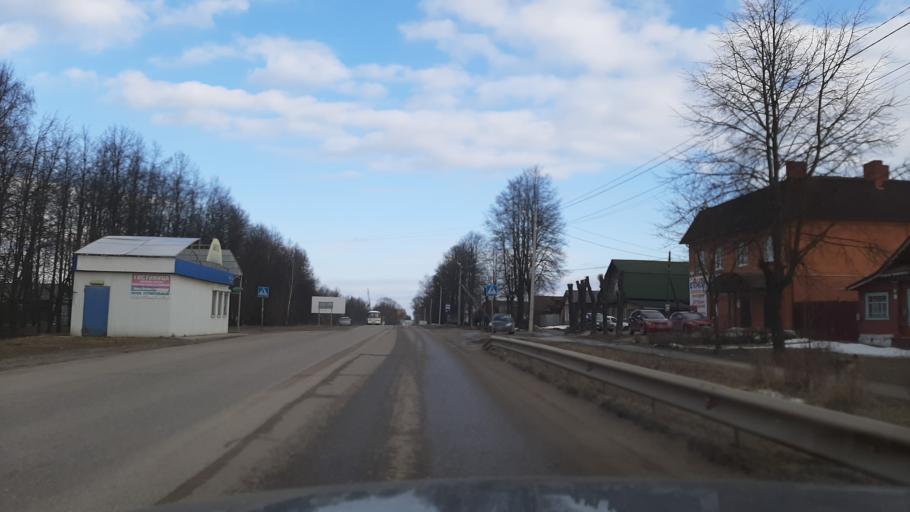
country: RU
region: Ivanovo
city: Teykovo
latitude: 56.8550
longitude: 40.5194
